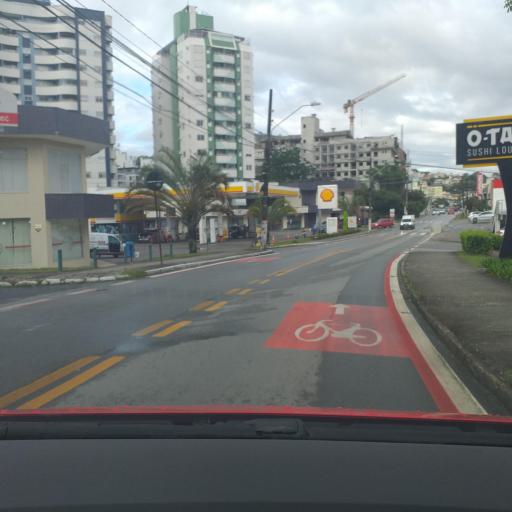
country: BR
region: Santa Catarina
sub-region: Florianopolis
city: Corrego Grande
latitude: -27.6005
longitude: -48.4994
